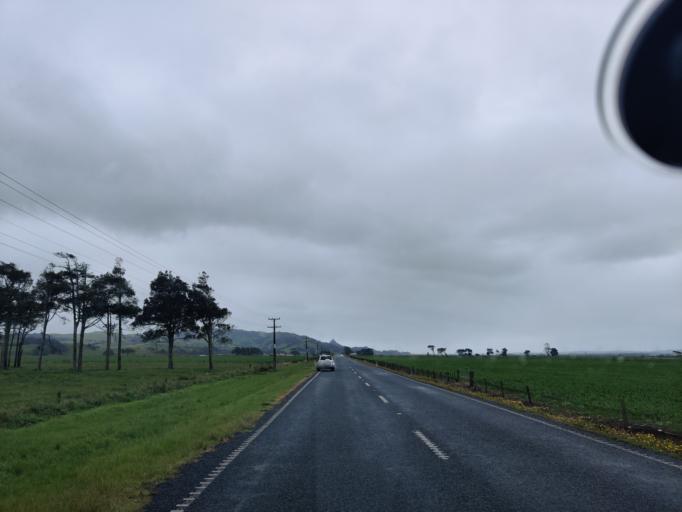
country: NZ
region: Northland
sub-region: Kaipara District
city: Dargaville
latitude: -36.0165
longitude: 173.9348
